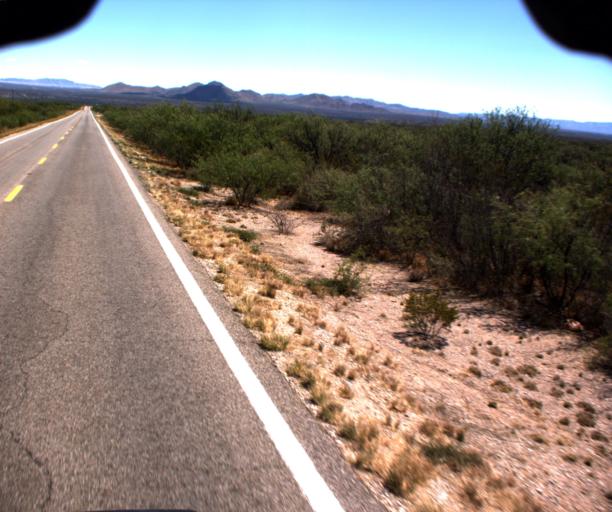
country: US
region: Arizona
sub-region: Cochise County
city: Huachuca City
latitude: 31.7199
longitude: -110.2342
